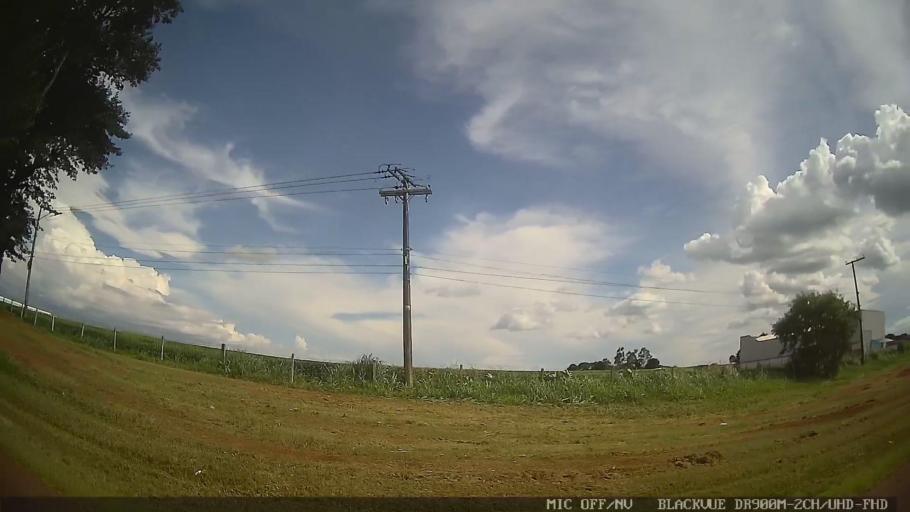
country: BR
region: Sao Paulo
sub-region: Laranjal Paulista
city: Laranjal Paulista
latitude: -23.0362
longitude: -47.8843
